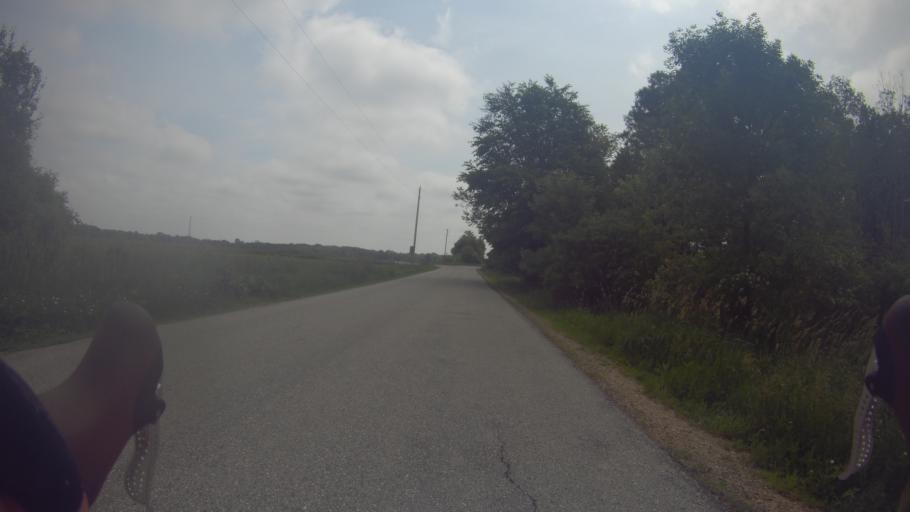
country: US
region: Wisconsin
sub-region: Jefferson County
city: Cambridge
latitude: 42.9237
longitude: -89.0049
